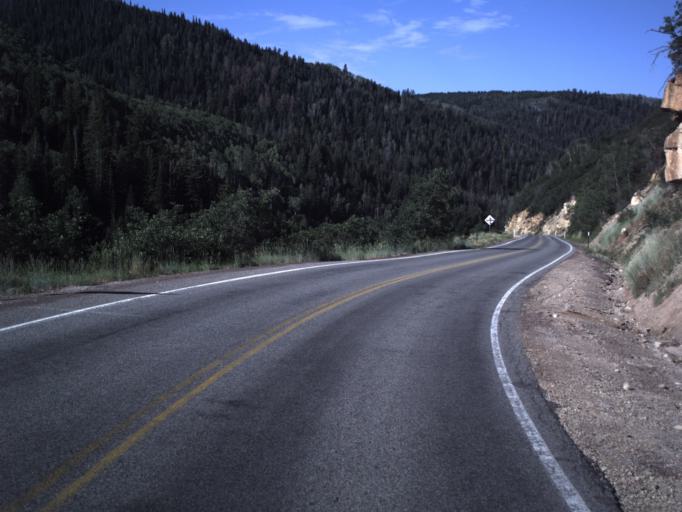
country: US
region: Utah
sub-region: Sanpete County
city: Fairview
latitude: 39.6530
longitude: -111.3550
